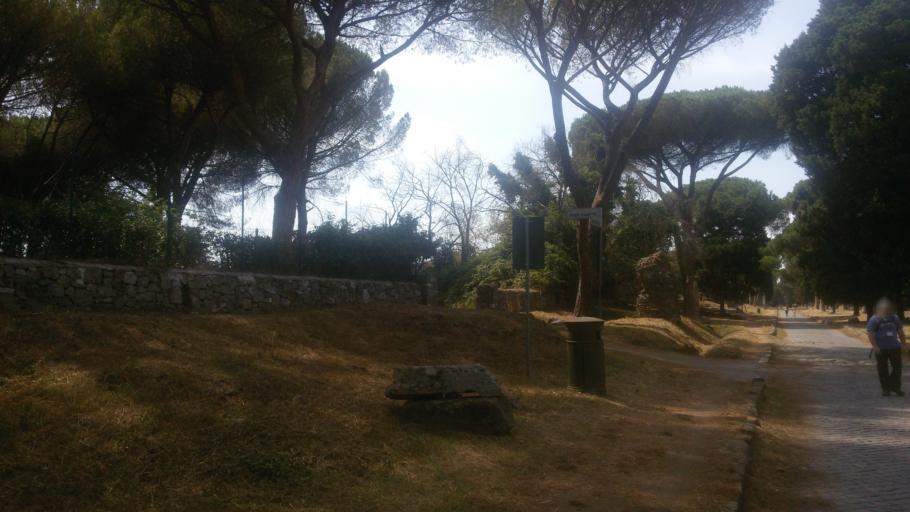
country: IT
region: Latium
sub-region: Citta metropolitana di Roma Capitale
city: Rome
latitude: 41.8366
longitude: 12.5380
